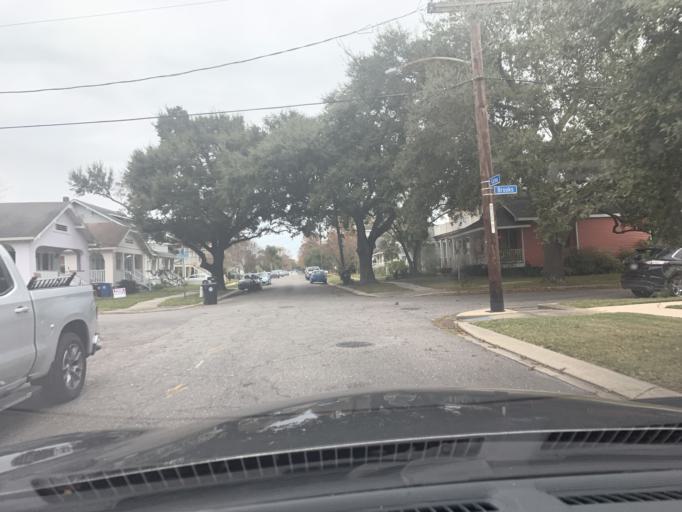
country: US
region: Louisiana
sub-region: Jefferson Parish
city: Metairie
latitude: 29.9972
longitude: -90.1142
